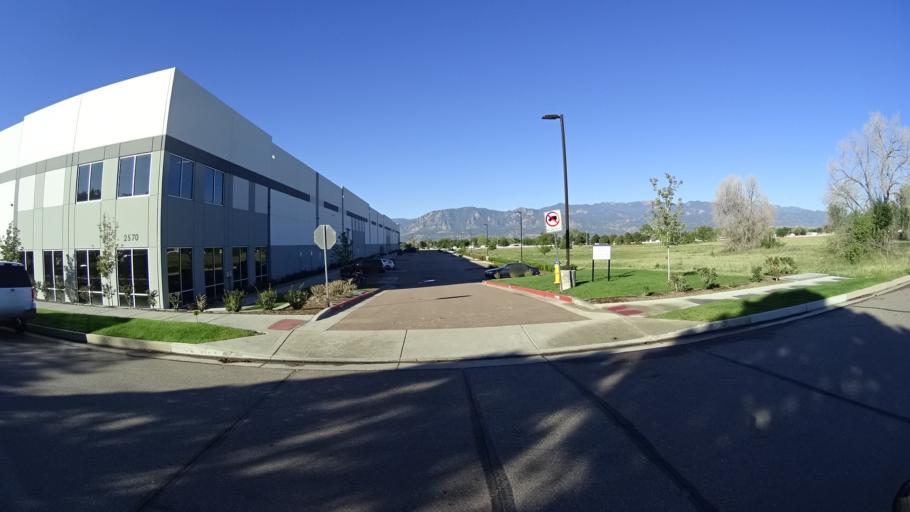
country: US
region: Colorado
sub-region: El Paso County
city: Security-Widefield
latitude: 38.7933
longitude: -104.7263
